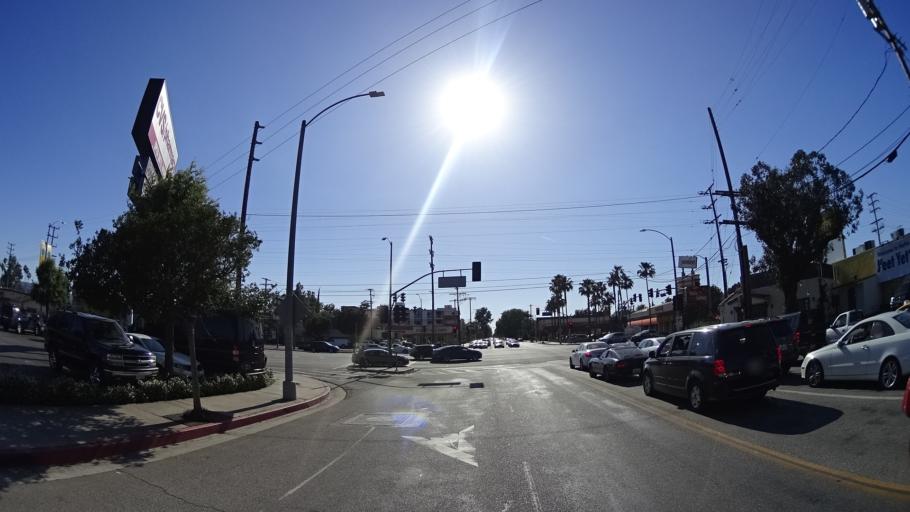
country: US
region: California
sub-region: Los Angeles County
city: North Hollywood
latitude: 34.1575
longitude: -118.3695
